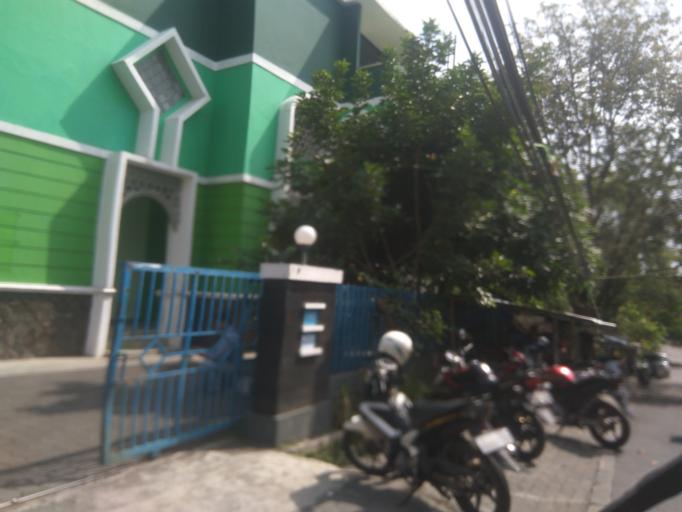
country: ID
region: Central Java
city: Semarang
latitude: -7.0531
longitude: 110.4358
